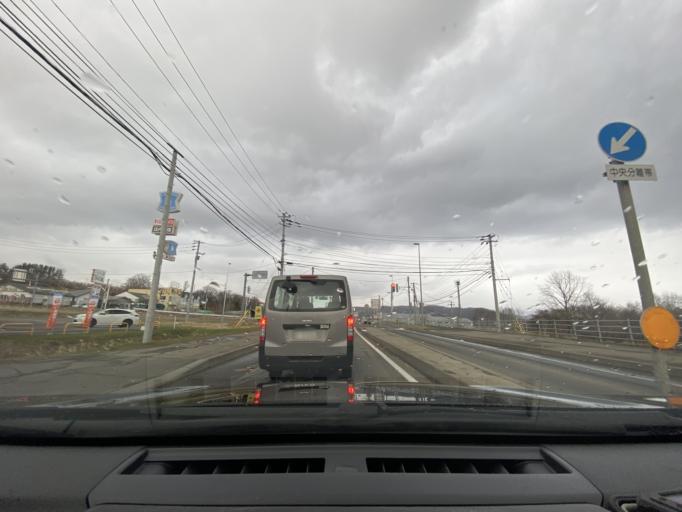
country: JP
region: Hokkaido
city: Otofuke
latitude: 43.2315
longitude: 143.5459
